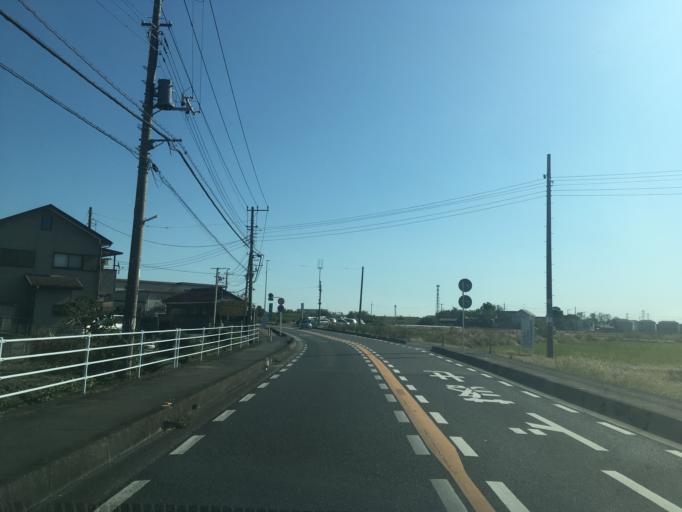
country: JP
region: Saitama
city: Kawagoe
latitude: 35.9434
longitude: 139.4633
